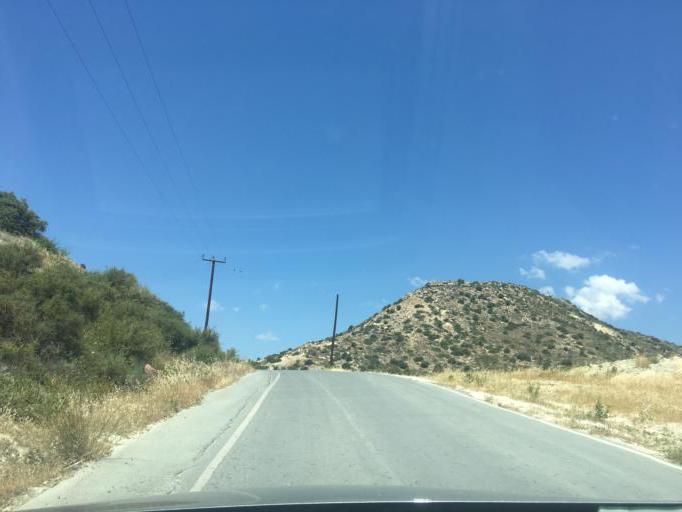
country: CY
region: Limassol
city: Mouttagiaka
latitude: 34.7235
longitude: 33.0749
